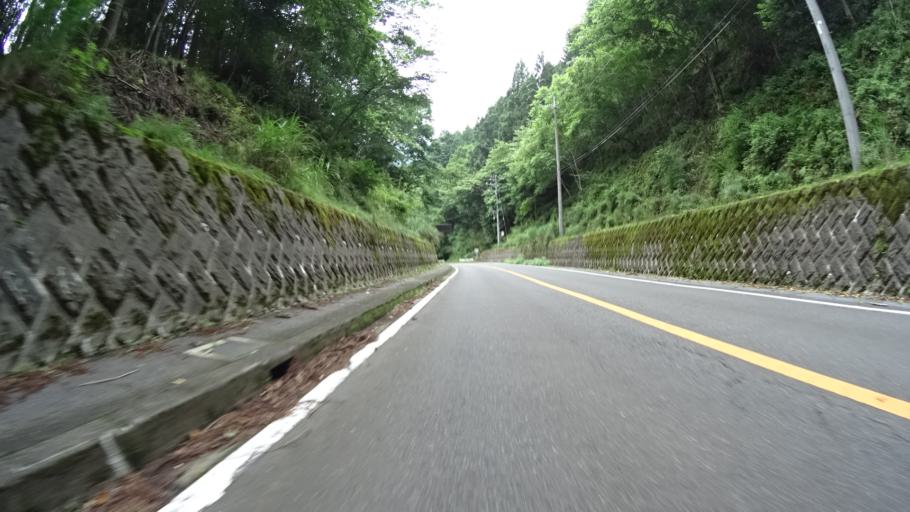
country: JP
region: Kanagawa
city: Hadano
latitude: 35.5035
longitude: 139.2297
